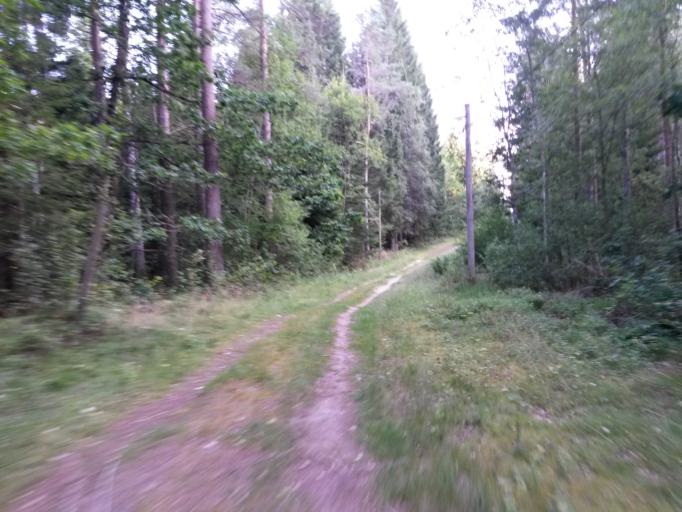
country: SE
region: Vaestra Goetaland
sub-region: Vargarda Kommun
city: Vargarda
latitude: 58.0389
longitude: 12.8413
